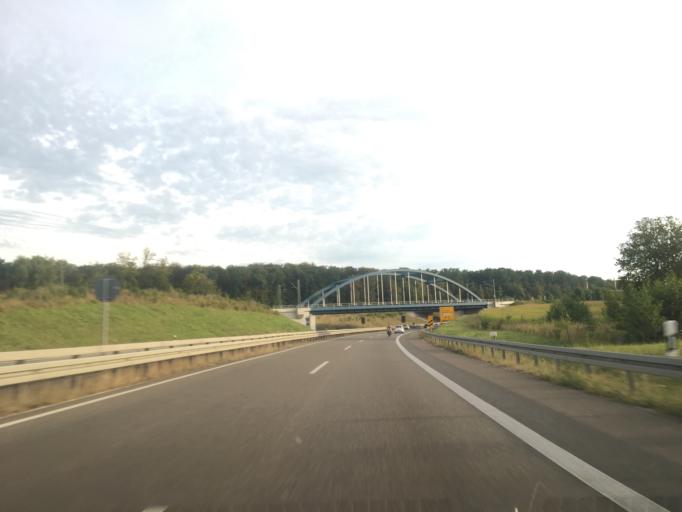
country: DE
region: Baden-Wuerttemberg
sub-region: Tuebingen Region
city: Metzingen
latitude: 48.5305
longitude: 9.2634
